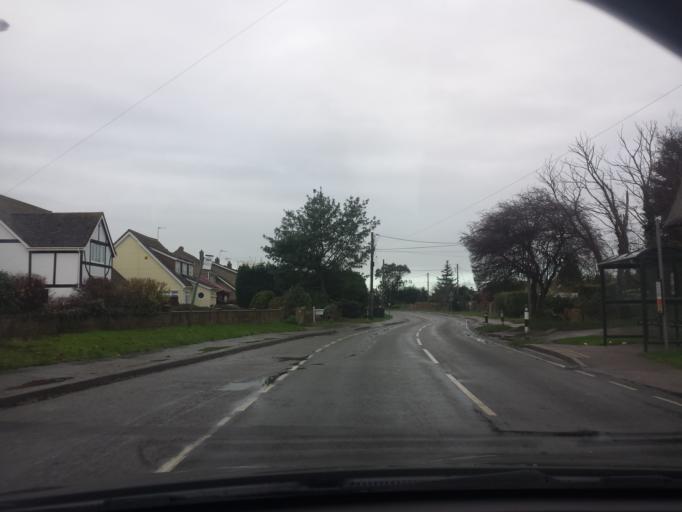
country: GB
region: England
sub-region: Essex
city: Saint Osyth
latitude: 51.7933
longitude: 1.0595
